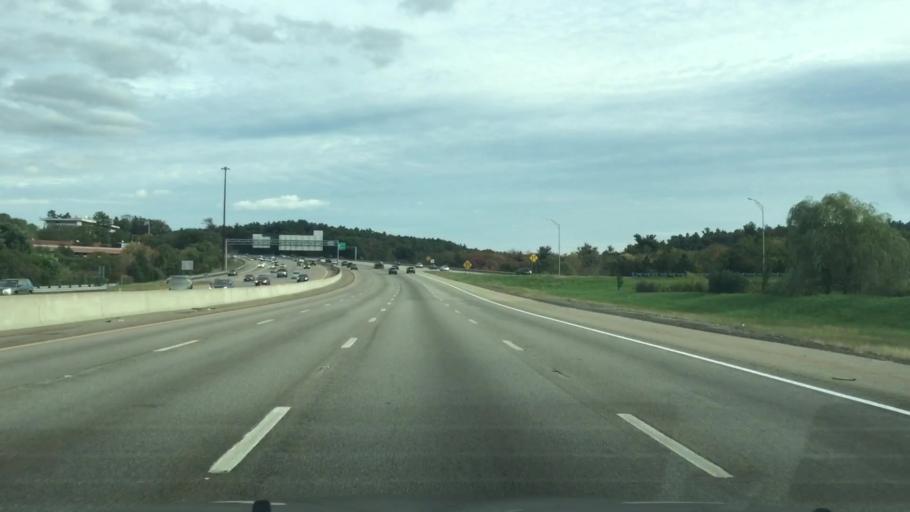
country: US
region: Massachusetts
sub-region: Norfolk County
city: Dedham
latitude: 42.2064
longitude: -71.1382
